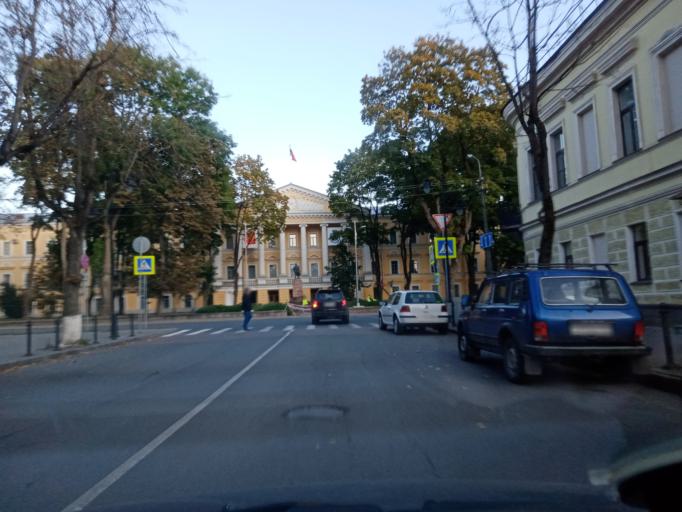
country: RU
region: Pskov
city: Pskov
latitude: 57.8162
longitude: 28.3407
